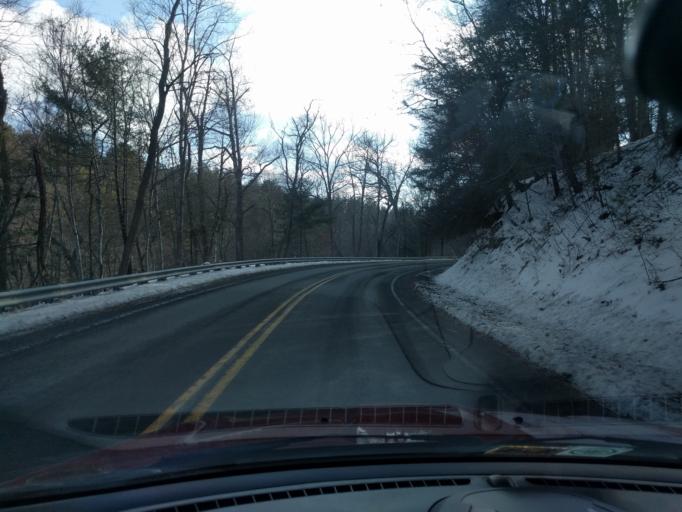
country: US
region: Virginia
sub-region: Bath County
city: Warm Springs
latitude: 38.0718
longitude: -79.8347
